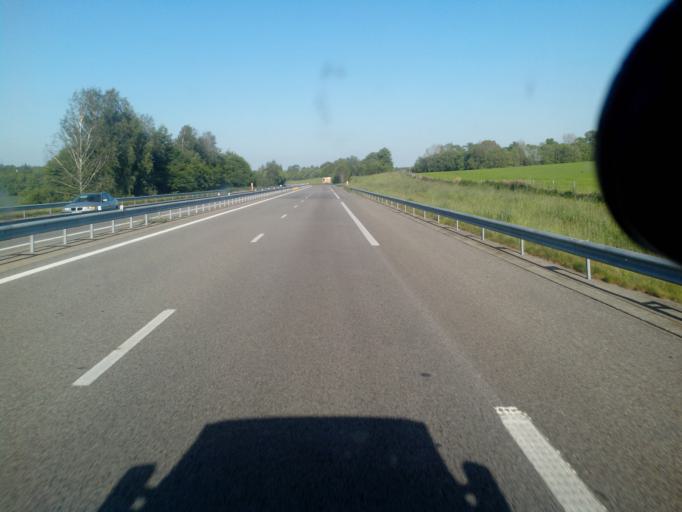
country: FR
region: Haute-Normandie
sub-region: Departement de la Seine-Maritime
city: La Remuee
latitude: 49.5693
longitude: 0.3853
